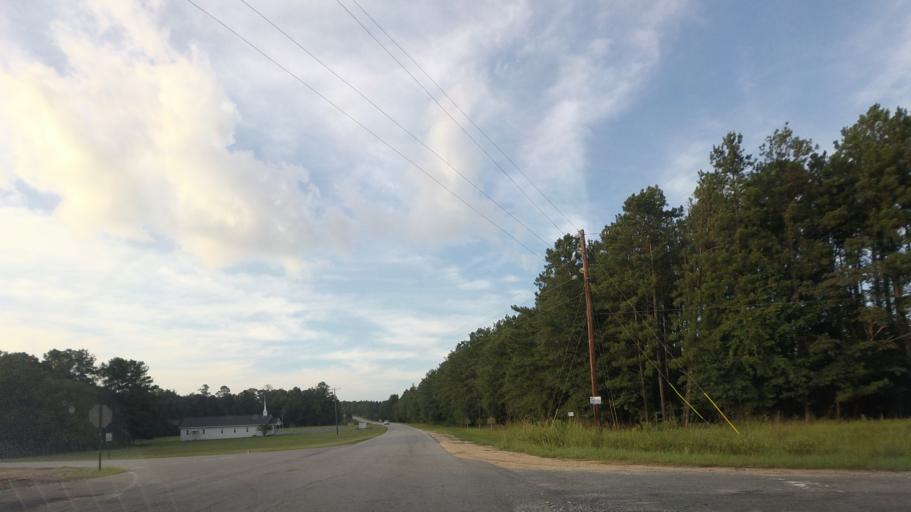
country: US
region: Georgia
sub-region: Jones County
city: Gray
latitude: 32.8705
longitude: -83.4890
